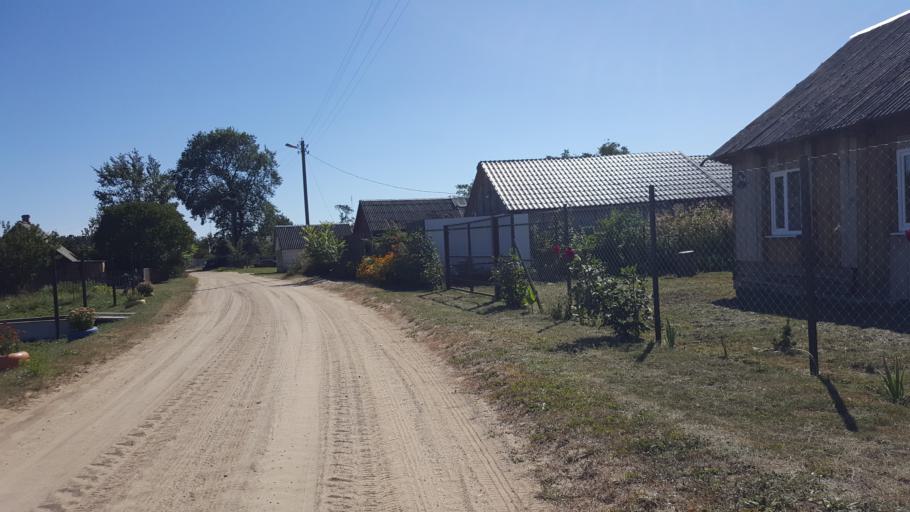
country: PL
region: Lublin Voivodeship
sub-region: Powiat bialski
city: Rokitno
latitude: 52.2196
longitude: 23.3420
